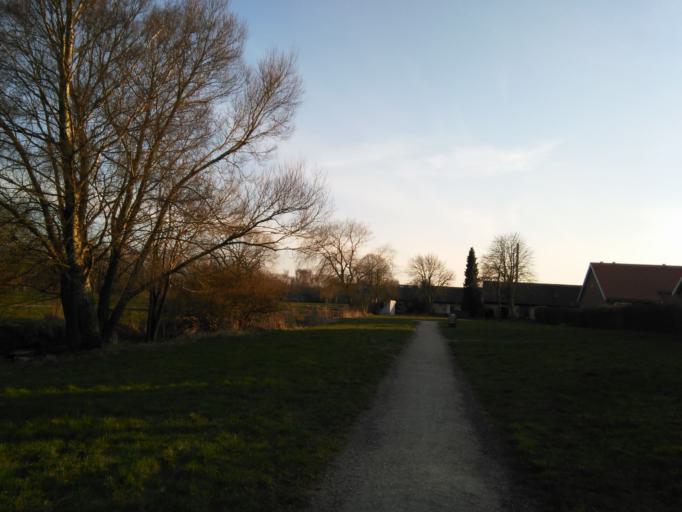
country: DK
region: Central Jutland
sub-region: Arhus Kommune
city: Beder
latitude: 56.0617
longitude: 10.2081
